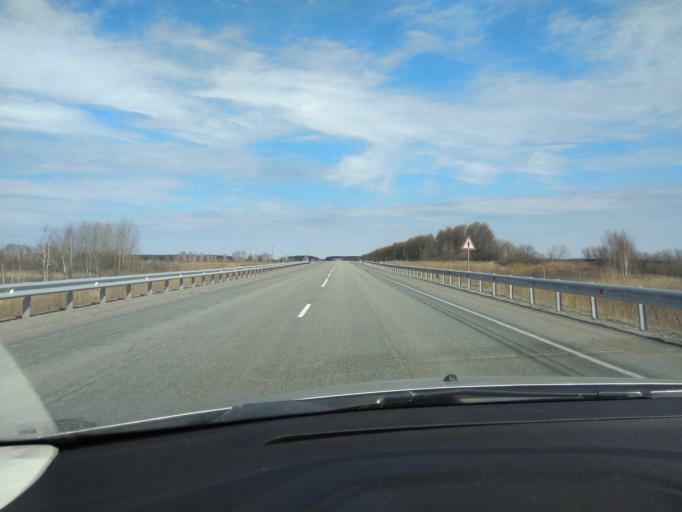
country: RU
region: Sverdlovsk
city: Troitskiy
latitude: 57.0861
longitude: 63.7105
